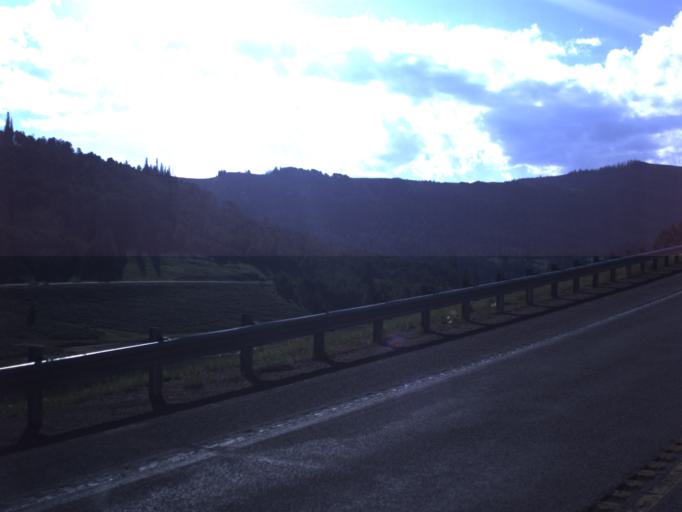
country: US
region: Utah
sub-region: Sanpete County
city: Fairview
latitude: 39.5855
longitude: -111.2427
